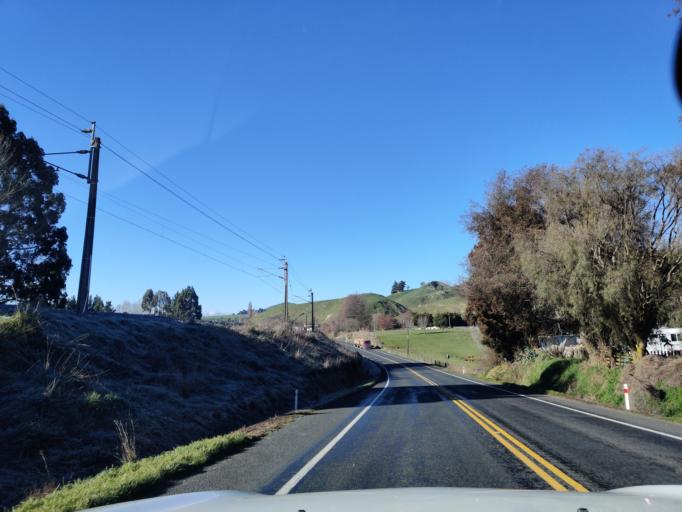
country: NZ
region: Manawatu-Wanganui
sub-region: Ruapehu District
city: Waiouru
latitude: -39.6876
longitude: 175.8077
